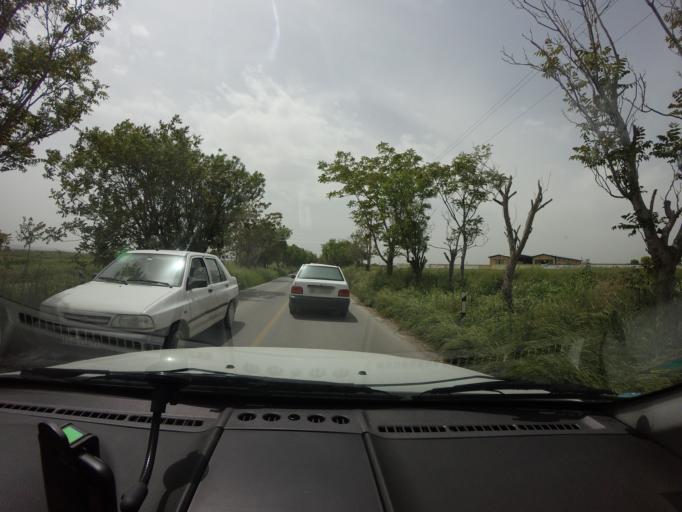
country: IR
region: Tehran
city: Eslamshahr
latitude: 35.5341
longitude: 51.2974
